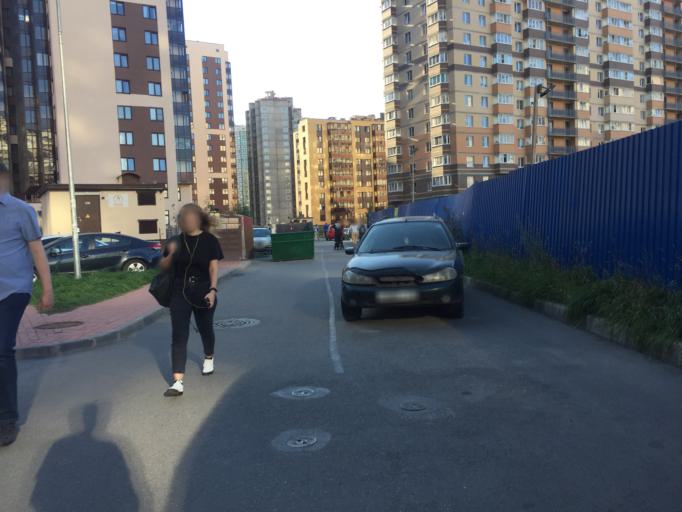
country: RU
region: Leningrad
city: Murino
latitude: 60.0541
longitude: 30.4333
